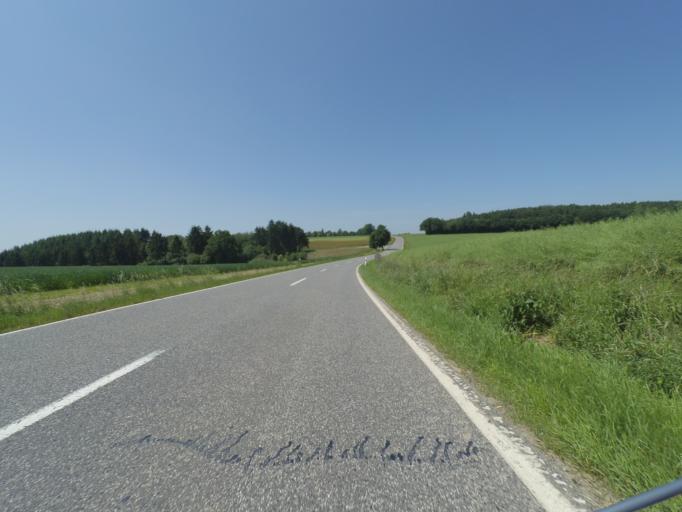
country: DE
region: Rheinland-Pfalz
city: Zilshausen
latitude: 50.1229
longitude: 7.3766
